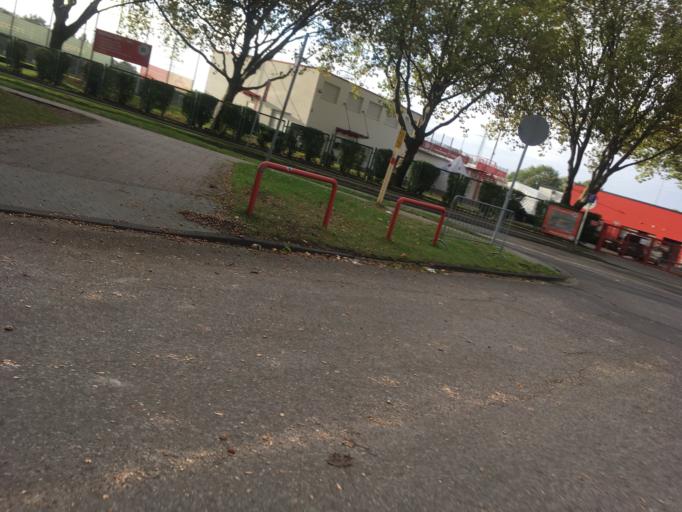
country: DE
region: North Rhine-Westphalia
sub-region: Regierungsbezirk Dusseldorf
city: Oberhausen
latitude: 51.4934
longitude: 6.8528
